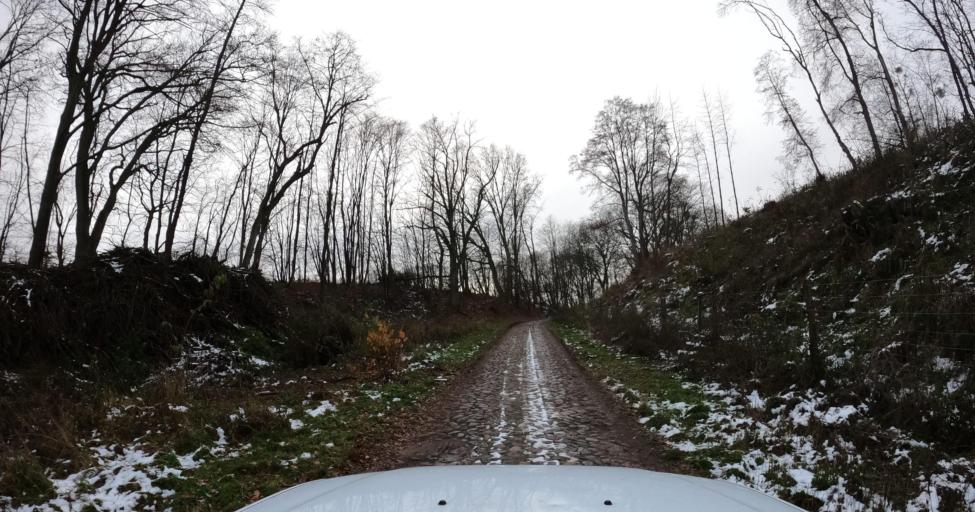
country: PL
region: West Pomeranian Voivodeship
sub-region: Powiat swidwinski
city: Rabino
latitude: 53.8904
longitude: 15.8889
